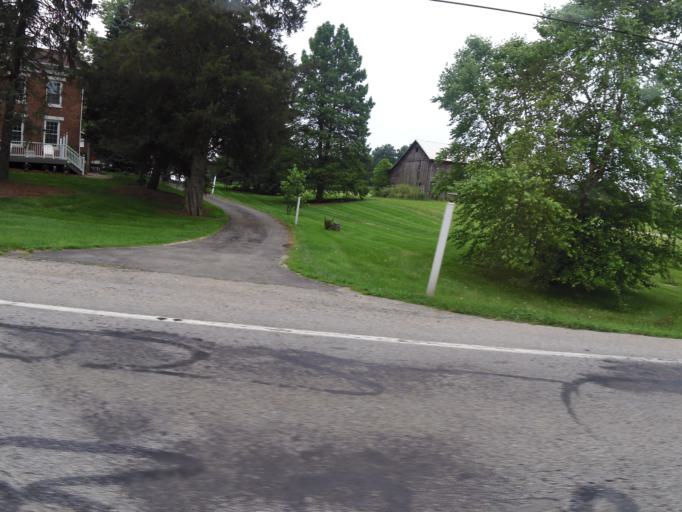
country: US
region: Ohio
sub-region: Clinton County
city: Wilmington
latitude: 39.4739
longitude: -83.8900
